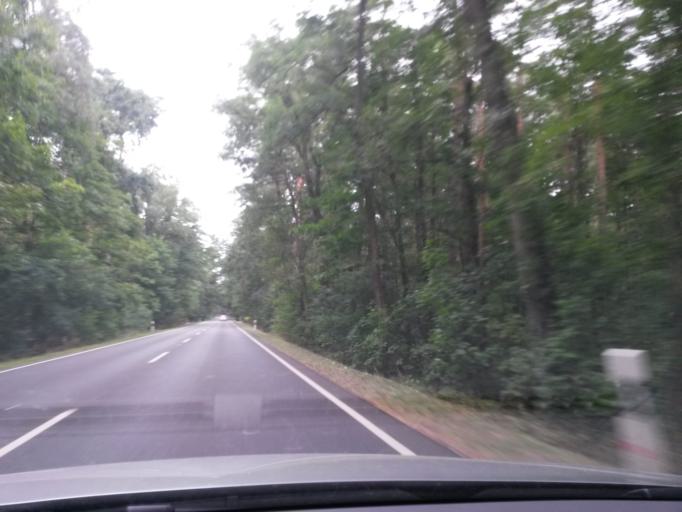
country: DE
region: Saxony-Anhalt
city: Klietz
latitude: 52.6344
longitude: 12.0477
